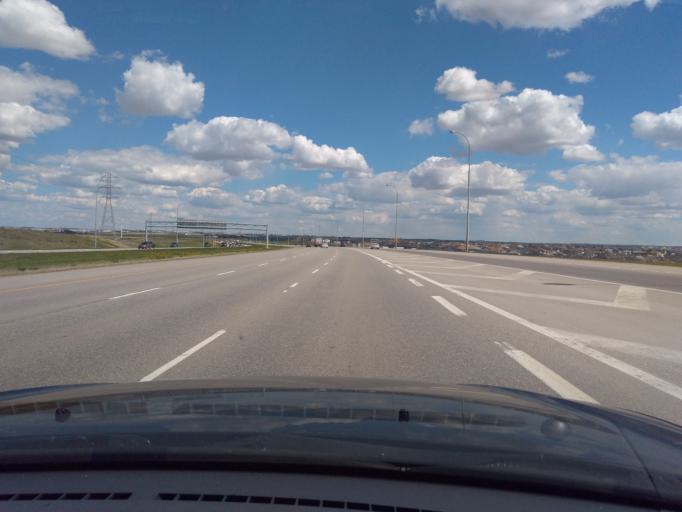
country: CA
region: Alberta
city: Calgary
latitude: 51.1728
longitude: -114.0624
